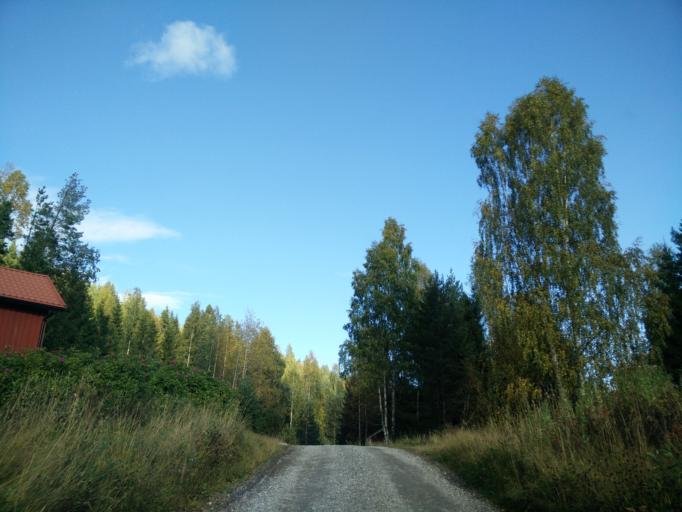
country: SE
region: Vaesternorrland
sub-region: Sundsvalls Kommun
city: Matfors
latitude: 62.3316
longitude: 16.9216
